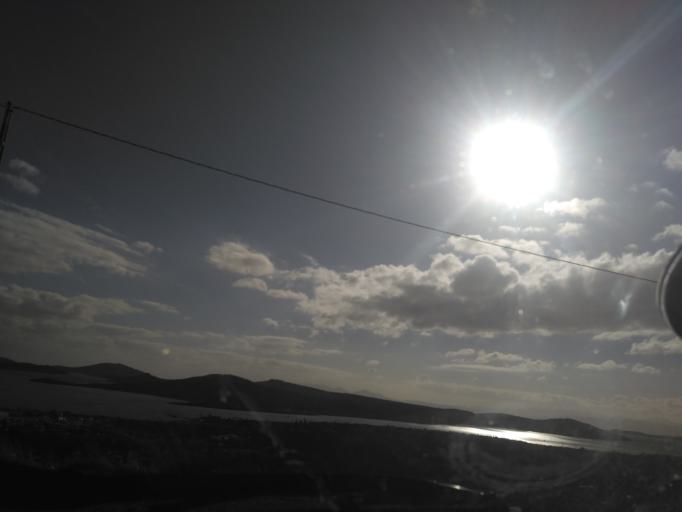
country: TR
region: Balikesir
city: Ayvalik
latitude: 39.3369
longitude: 26.6522
